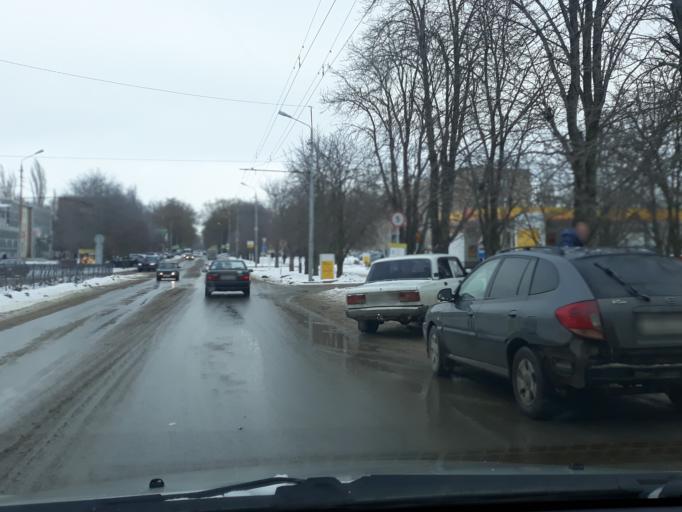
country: RU
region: Rostov
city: Taganrog
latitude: 47.2522
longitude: 38.9179
